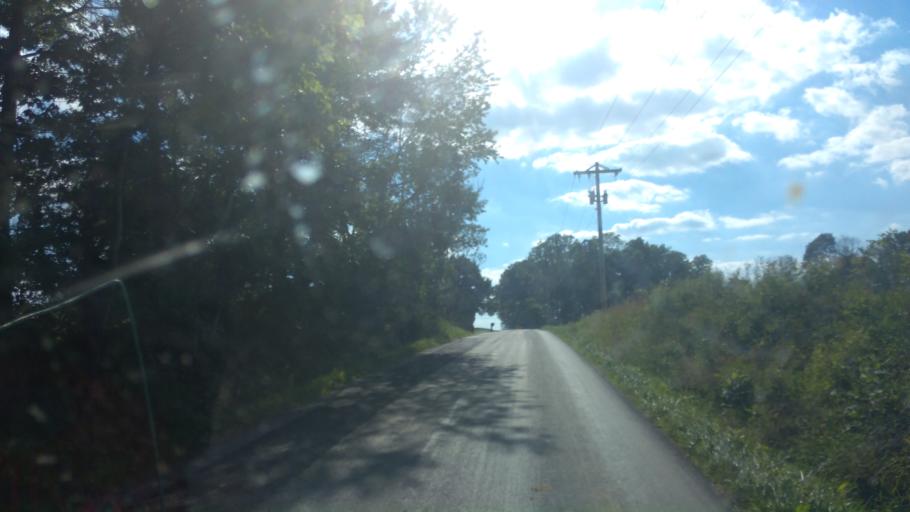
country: US
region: Ohio
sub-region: Wayne County
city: Apple Creek
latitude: 40.7262
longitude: -81.8932
